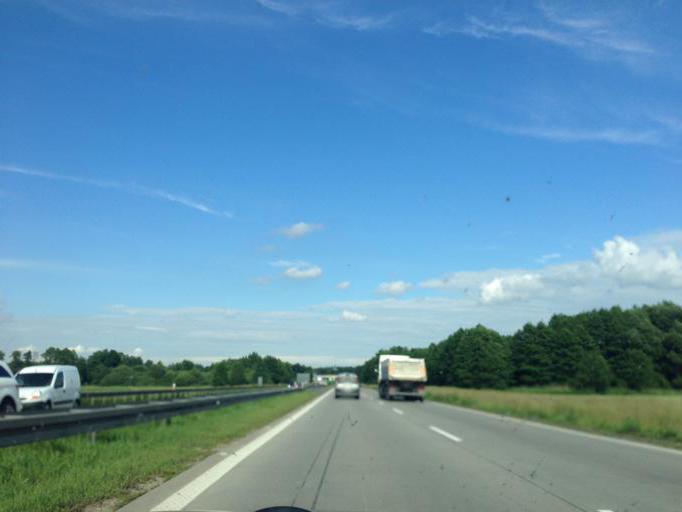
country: PL
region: Lower Silesian Voivodeship
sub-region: Powiat wroclawski
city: Katy Wroclawskie
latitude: 51.0216
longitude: 16.7654
